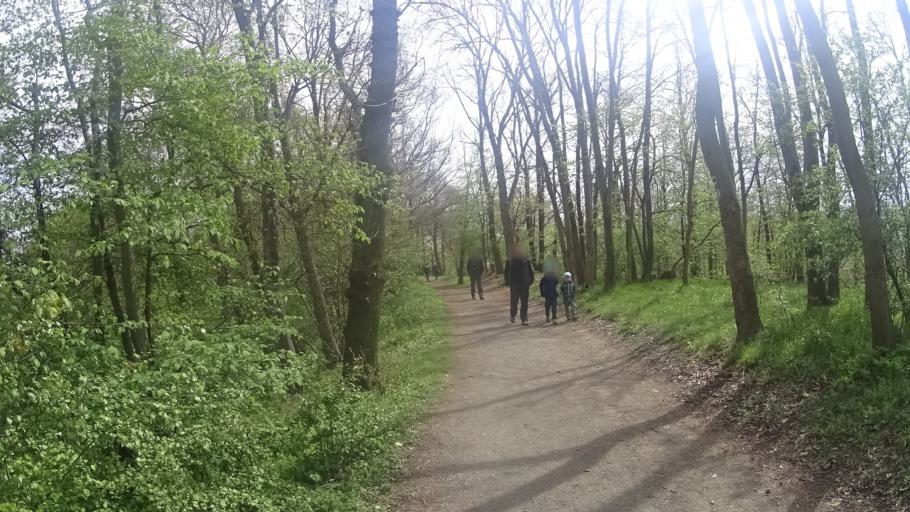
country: DE
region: Thuringia
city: Wandersleben
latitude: 50.8679
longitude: 10.8341
